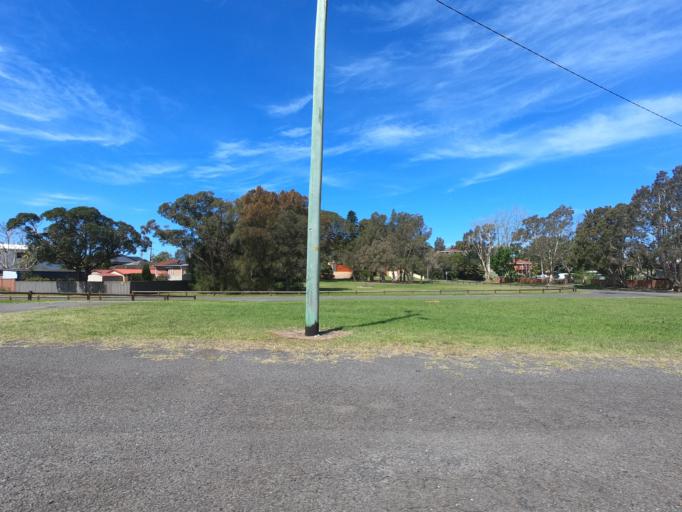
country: AU
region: New South Wales
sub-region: Wollongong
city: Lake Heights
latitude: -34.5004
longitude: 150.8735
